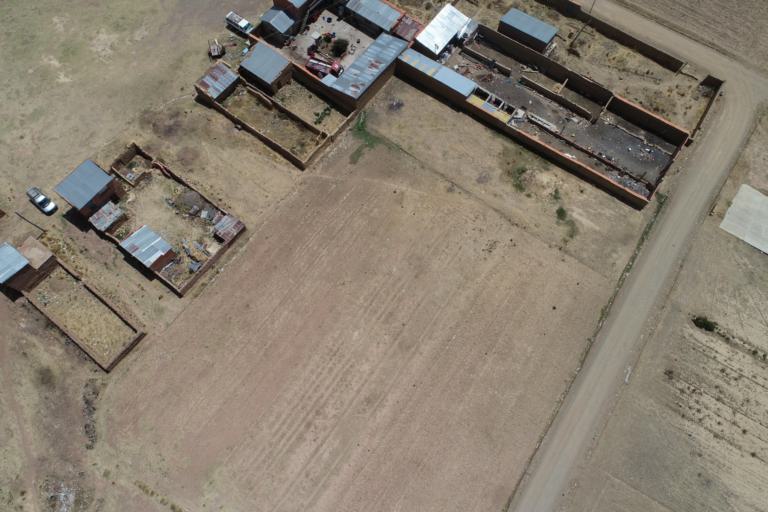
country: BO
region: La Paz
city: Achacachi
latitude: -15.9130
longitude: -68.8873
